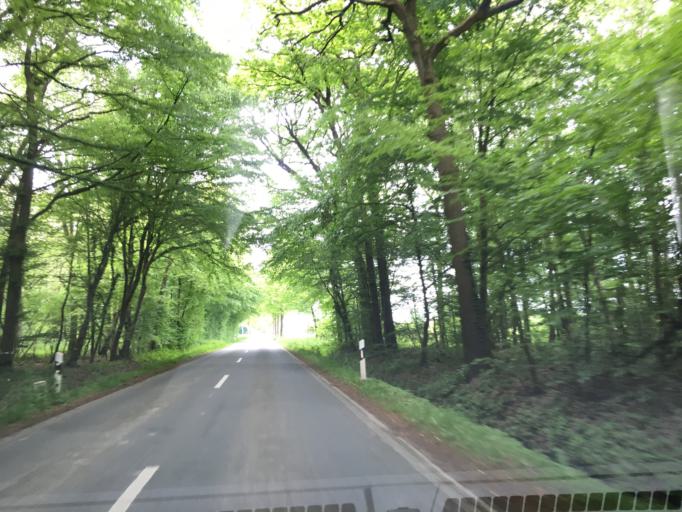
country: DE
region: North Rhine-Westphalia
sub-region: Regierungsbezirk Munster
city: Altenberge
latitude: 51.9836
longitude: 7.5086
